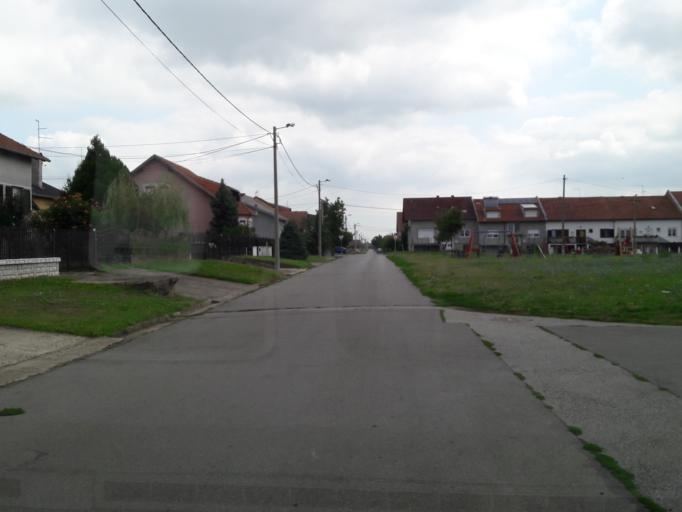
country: HR
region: Osjecko-Baranjska
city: Tenja
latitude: 45.5190
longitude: 18.7257
